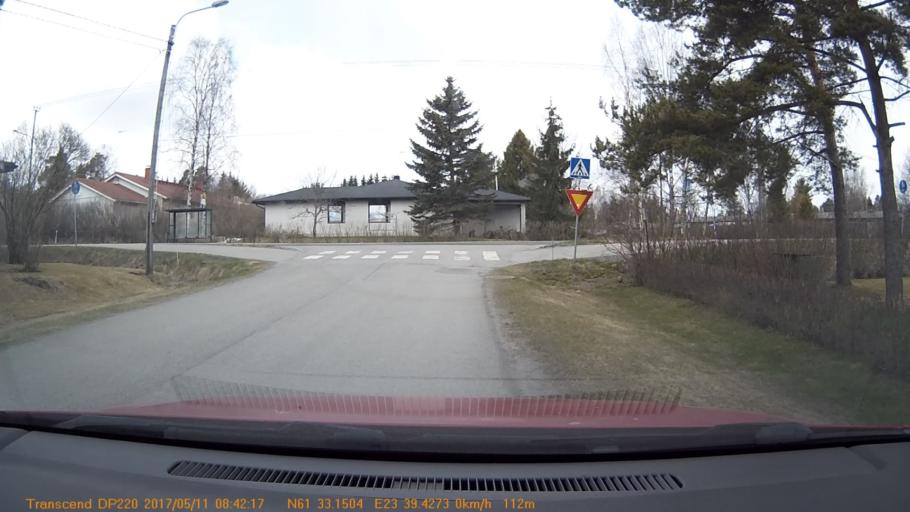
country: FI
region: Pirkanmaa
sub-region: Tampere
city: Yloejaervi
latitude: 61.5525
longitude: 23.6571
